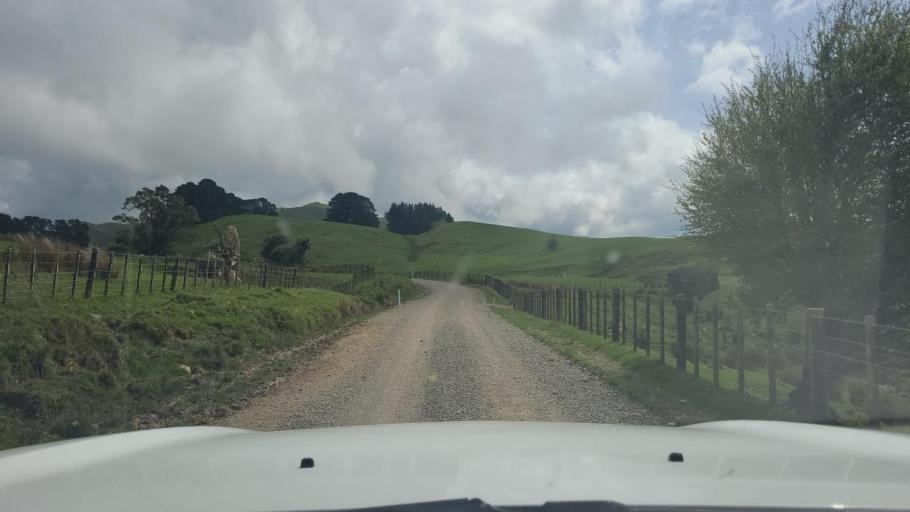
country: NZ
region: Wellington
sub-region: Masterton District
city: Masterton
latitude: -40.9237
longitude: 175.5400
